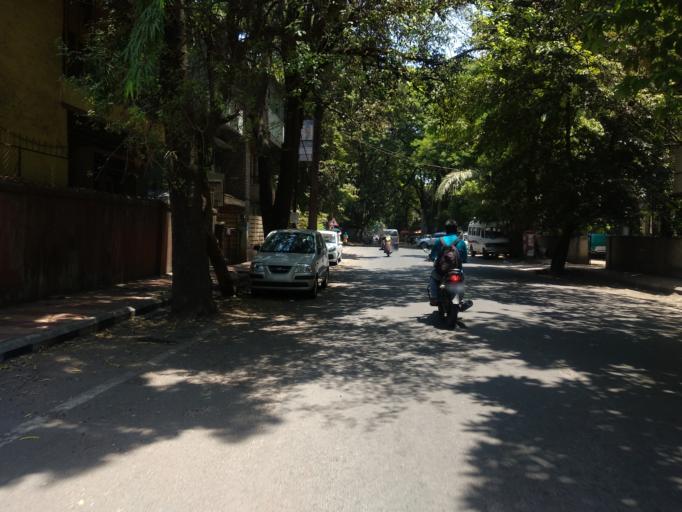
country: IN
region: Maharashtra
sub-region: Pune Division
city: Pune
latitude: 18.5054
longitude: 73.8507
